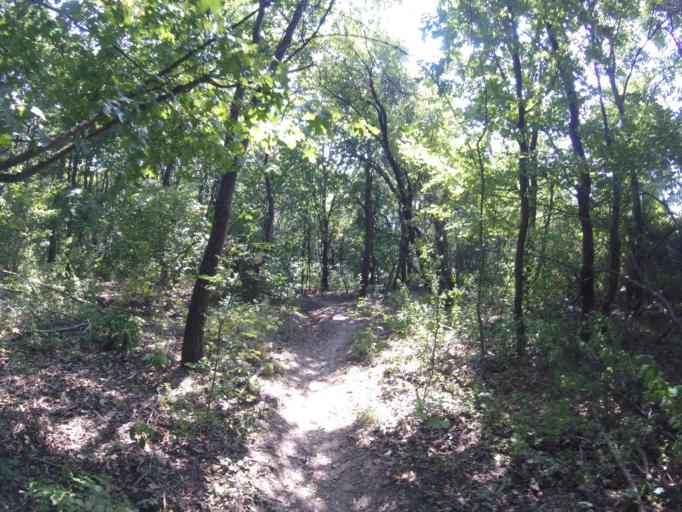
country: HU
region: Pest
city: Csobanka
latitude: 47.6695
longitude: 18.9645
